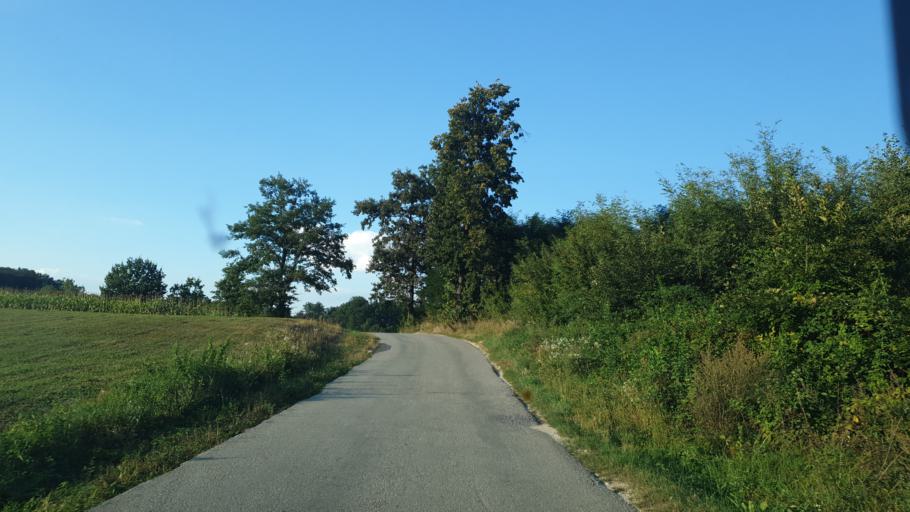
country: RS
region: Central Serbia
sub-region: Zlatiborski Okrug
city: Pozega
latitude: 43.8618
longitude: 19.9840
